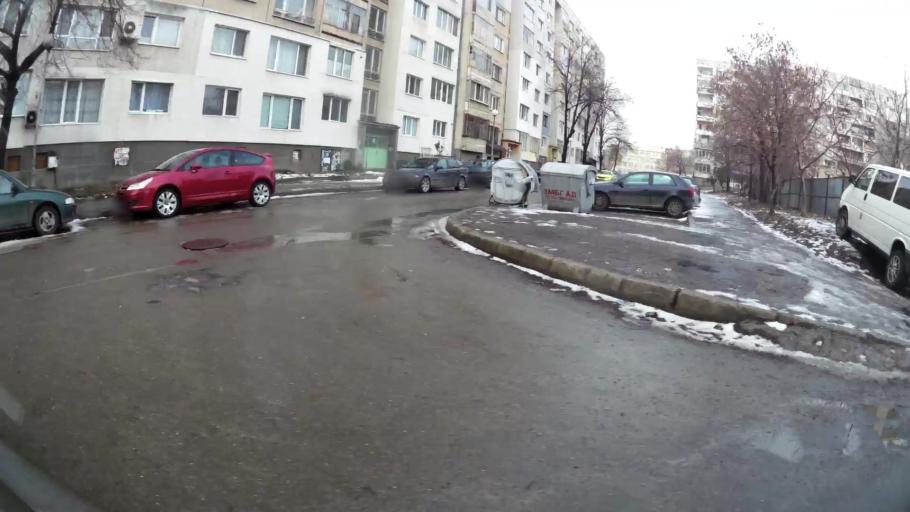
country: BG
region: Sofia-Capital
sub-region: Stolichna Obshtina
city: Sofia
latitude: 42.7109
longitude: 23.2654
